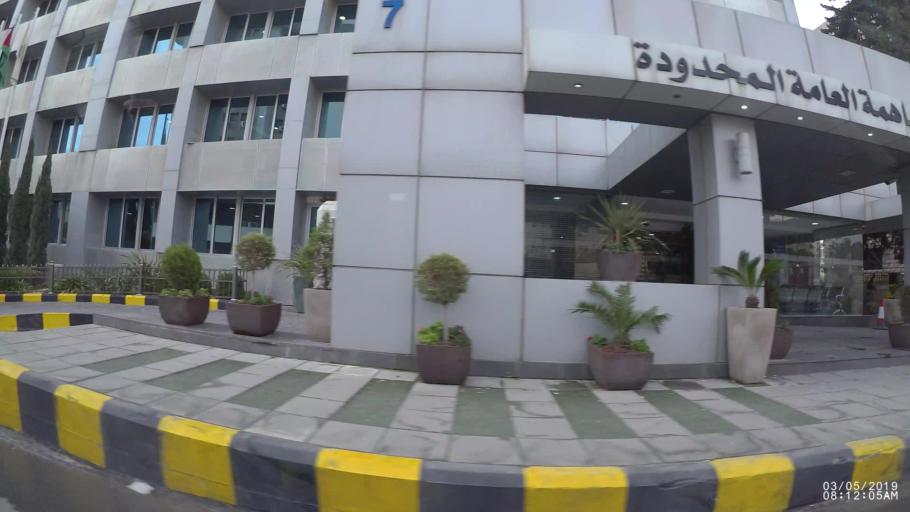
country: JO
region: Amman
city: Amman
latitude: 31.9690
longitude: 35.9072
